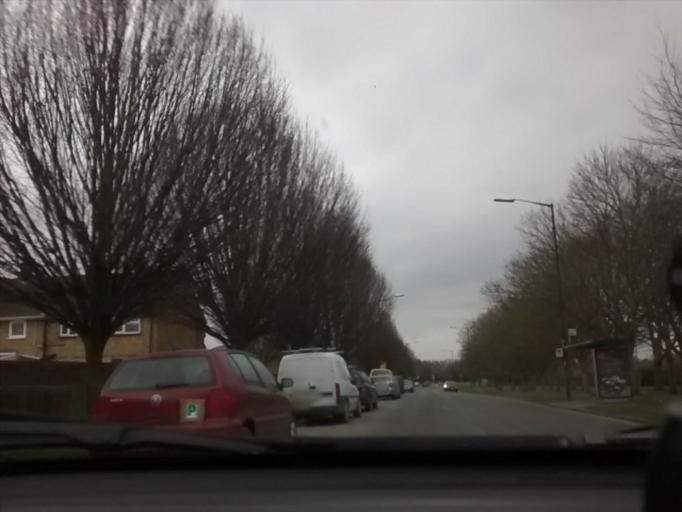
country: GB
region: England
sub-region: Cambridgeshire
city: Cambridge
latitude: 52.2089
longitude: 0.1634
